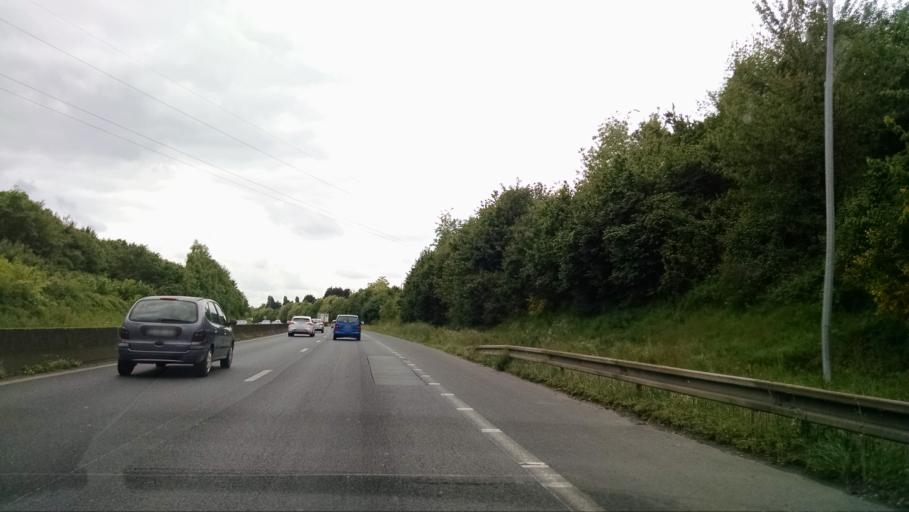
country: FR
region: Pays de la Loire
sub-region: Departement de la Loire-Atlantique
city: La Chapelle-sur-Erdre
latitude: 47.2680
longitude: -1.5723
